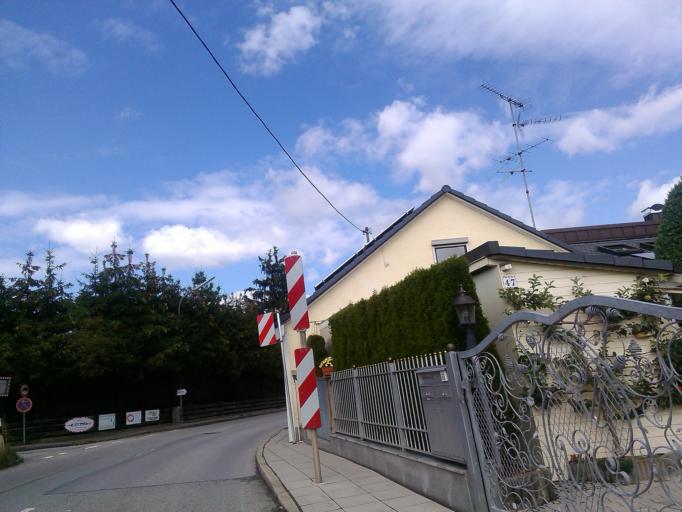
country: DE
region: Bavaria
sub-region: Upper Bavaria
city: Gilching
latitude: 48.1017
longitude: 11.3075
